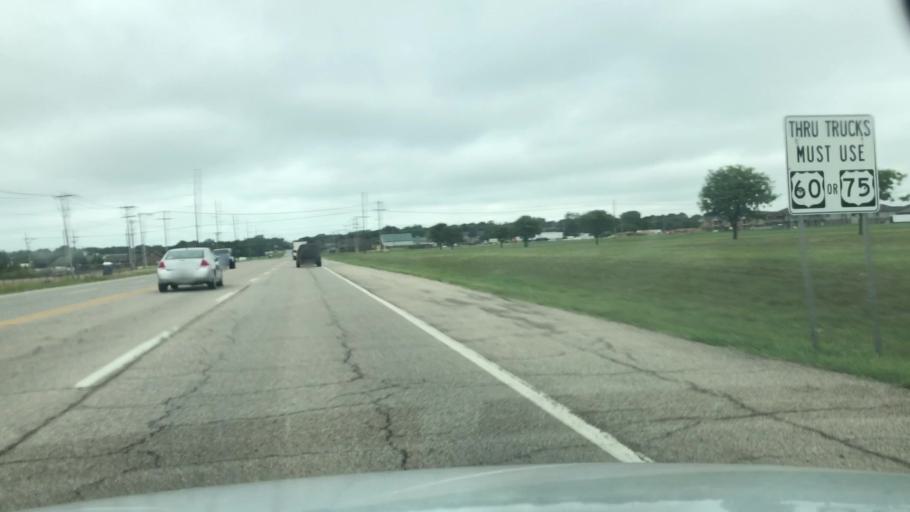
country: US
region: Oklahoma
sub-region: Washington County
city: Dewey
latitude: 36.7280
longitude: -95.8967
